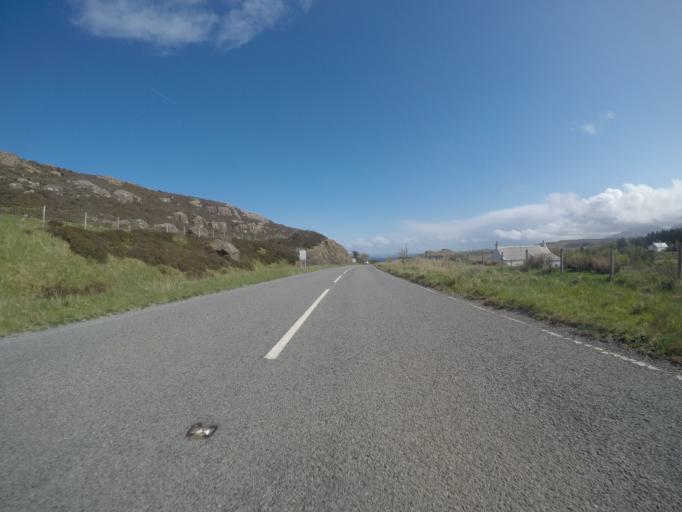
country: GB
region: Scotland
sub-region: Highland
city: Portree
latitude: 57.6136
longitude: -6.1800
